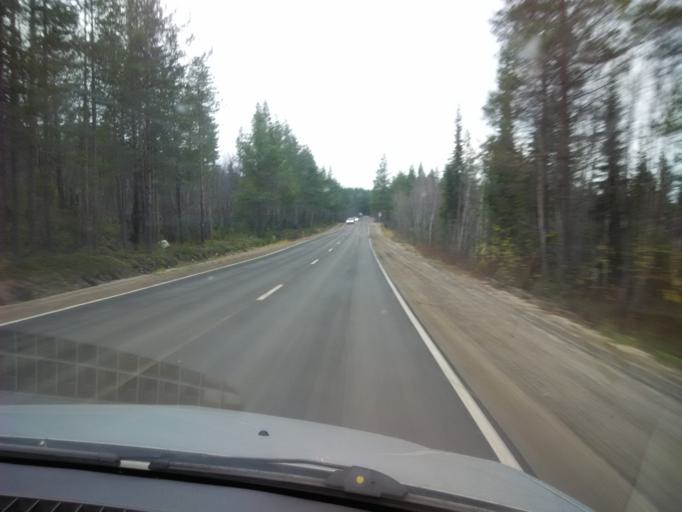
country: RU
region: Murmansk
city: Kandalaksha
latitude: 67.2337
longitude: 32.4100
